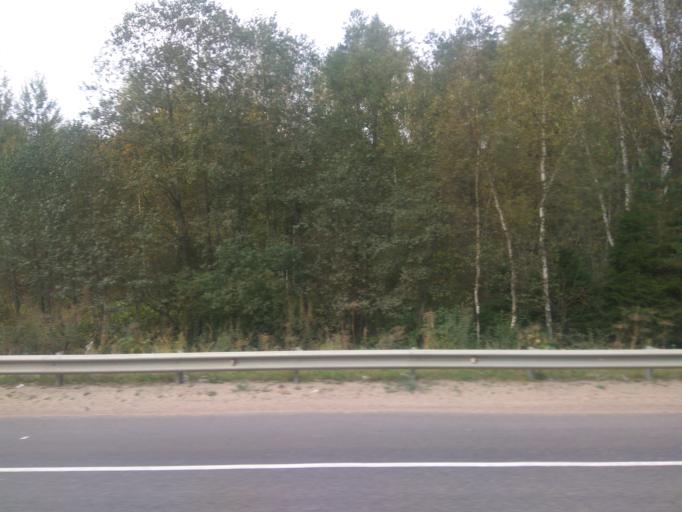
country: RU
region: Moskovskaya
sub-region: Shchelkovskiy Rayon
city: Grebnevo
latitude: 56.0015
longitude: 38.1294
